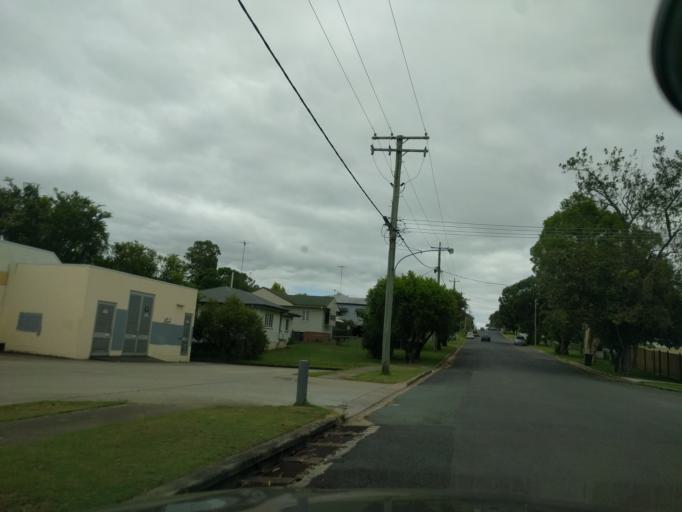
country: AU
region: Queensland
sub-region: Logan
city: Cedar Vale
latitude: -27.9891
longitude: 153.0002
